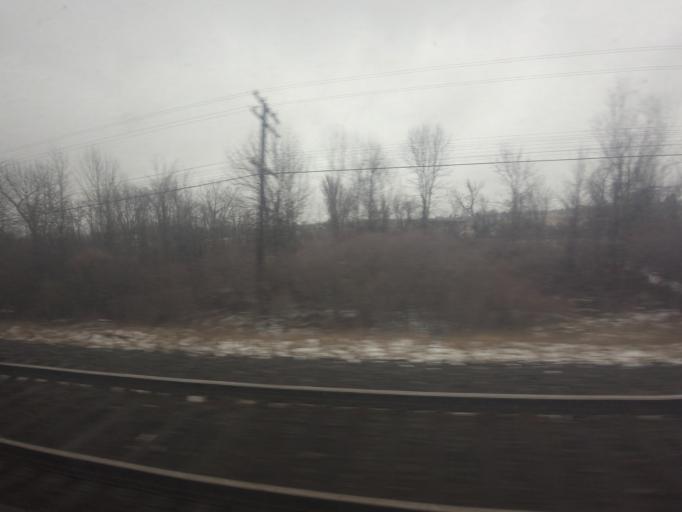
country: CA
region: Ontario
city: Quinte West
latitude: 44.0655
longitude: -77.6690
